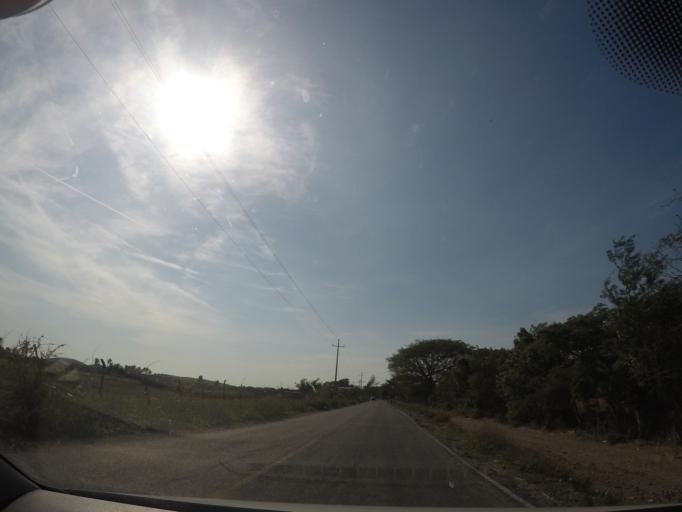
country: MX
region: Oaxaca
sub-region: Salina Cruz
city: Salina Cruz
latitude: 16.2211
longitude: -95.1324
